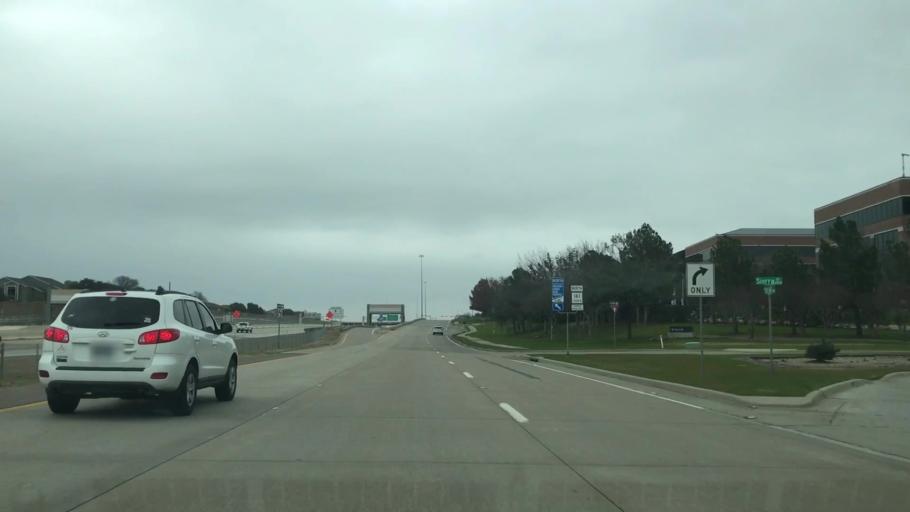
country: US
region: Texas
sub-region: Dallas County
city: Farmers Branch
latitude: 32.8999
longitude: -96.9650
